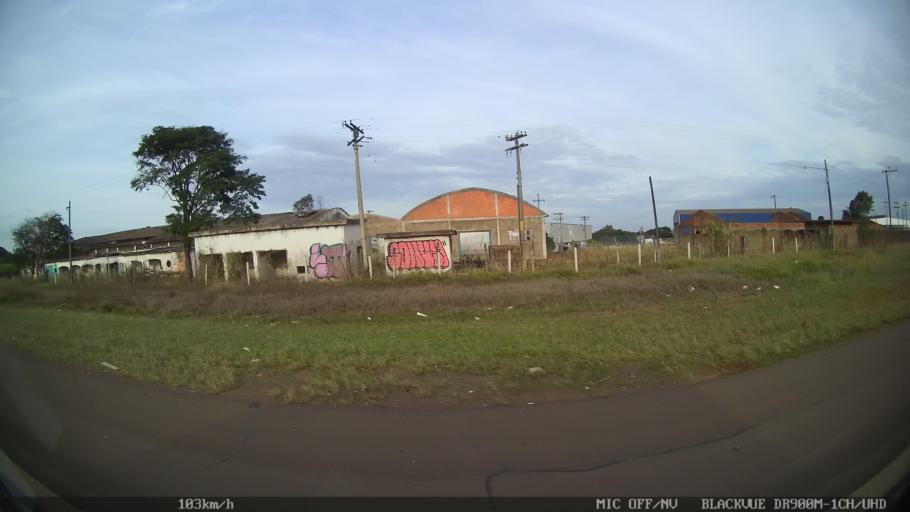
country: BR
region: Sao Paulo
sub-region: Iracemapolis
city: Iracemapolis
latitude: -22.6047
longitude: -47.4742
